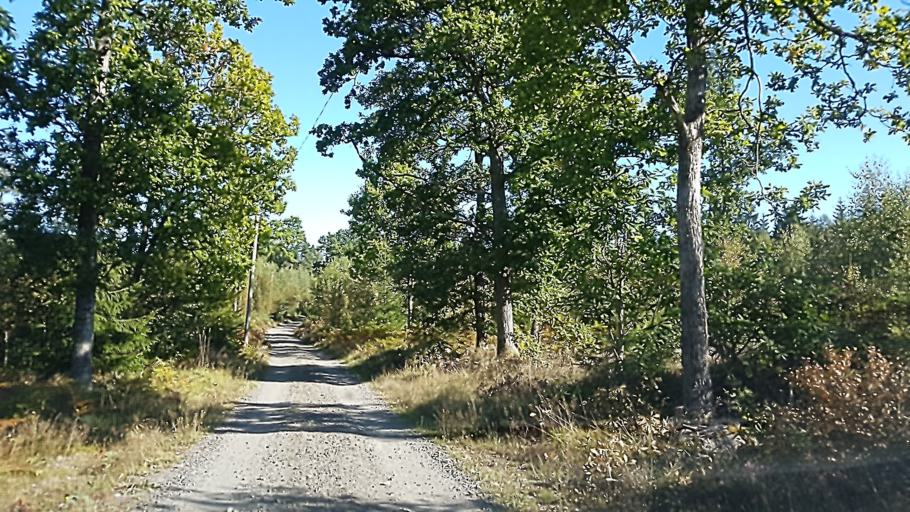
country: SE
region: Kronoberg
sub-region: Ljungby Kommun
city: Ljungby
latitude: 56.8084
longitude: 14.0023
